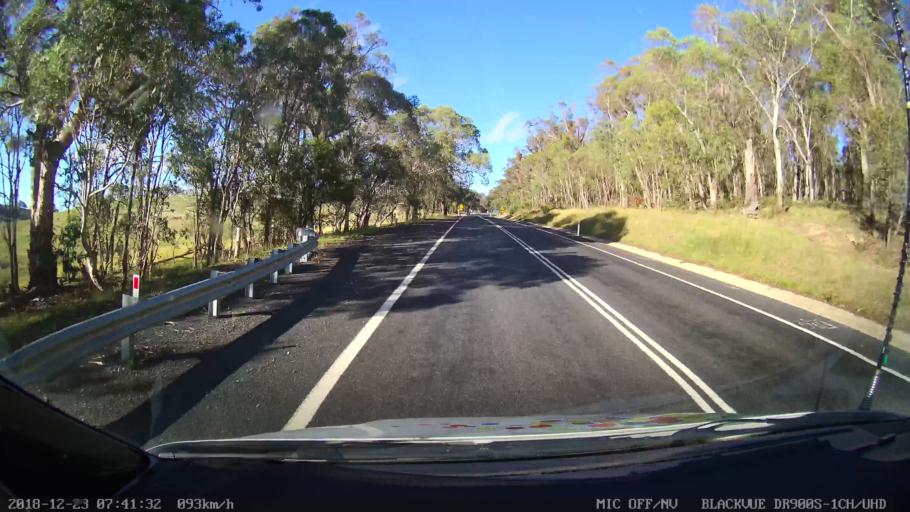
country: AU
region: New South Wales
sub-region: Armidale Dumaresq
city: Enmore
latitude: -30.5145
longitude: 151.9913
